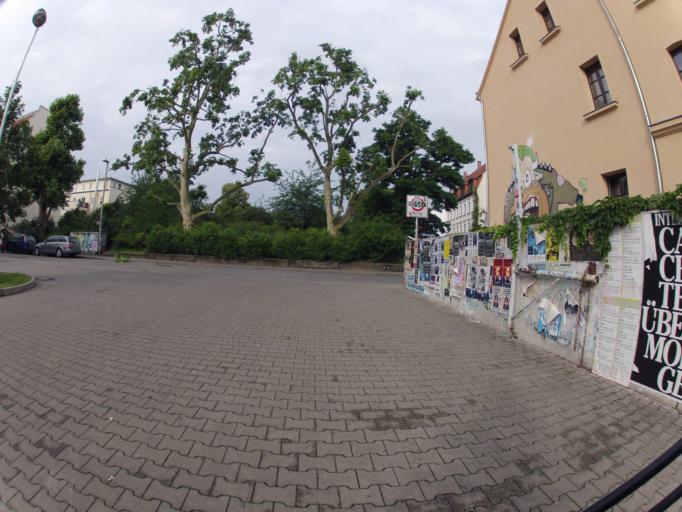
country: DE
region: Saxony
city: Leipzig
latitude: 51.3082
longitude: 12.3757
